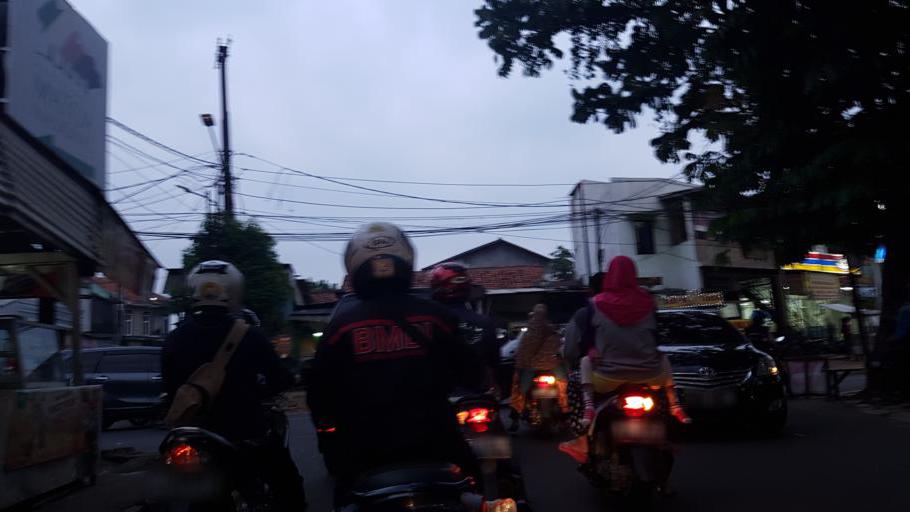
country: ID
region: West Java
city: Depok
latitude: -6.3628
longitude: 106.8018
